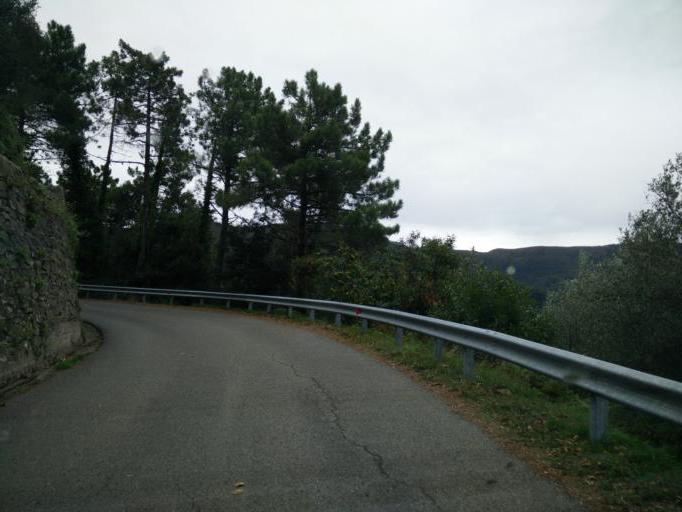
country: IT
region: Liguria
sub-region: Provincia di La Spezia
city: Vernazza
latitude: 44.1447
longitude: 9.6854
